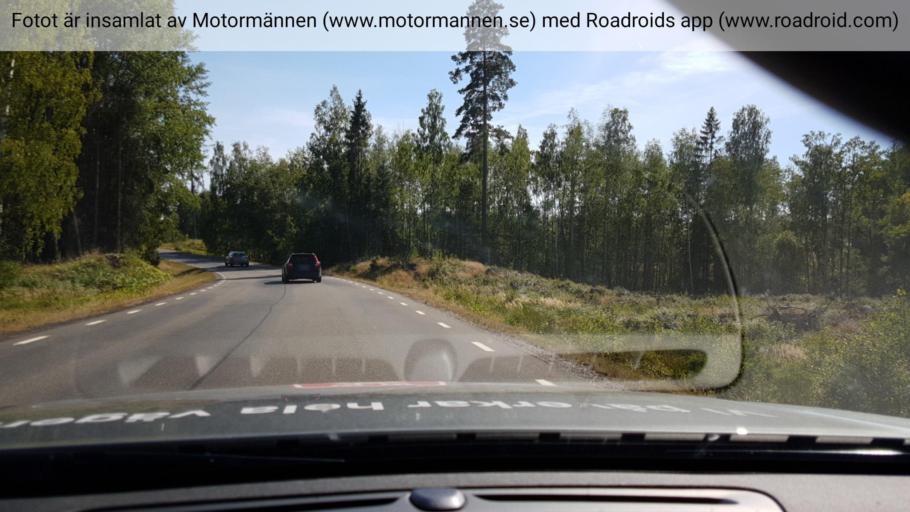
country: SE
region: Vaestra Goetaland
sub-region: Toreboda Kommun
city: Toereboda
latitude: 58.6775
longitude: 14.3118
